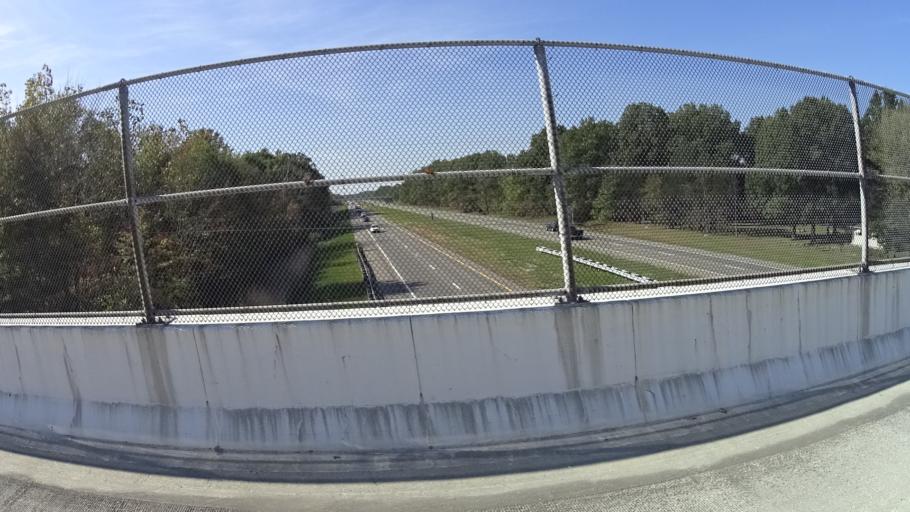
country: US
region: Ohio
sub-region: Lorain County
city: Vermilion-on-the-Lake
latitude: 41.4035
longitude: -82.2967
